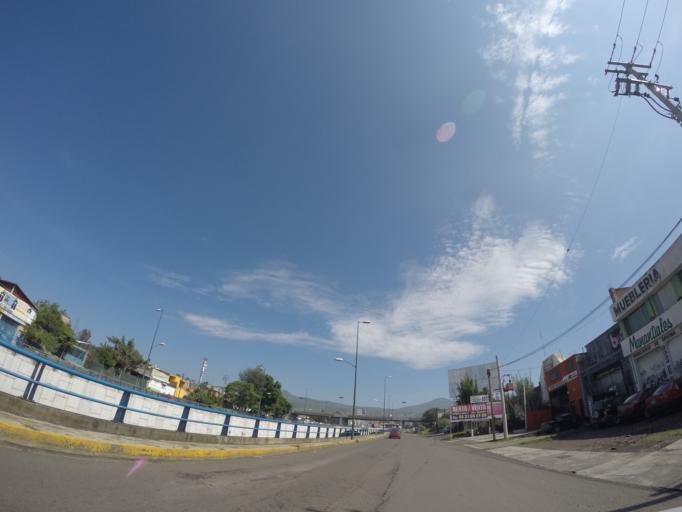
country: MX
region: Michoacan
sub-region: Morelia
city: San Antonio
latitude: 19.6985
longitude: -101.2425
